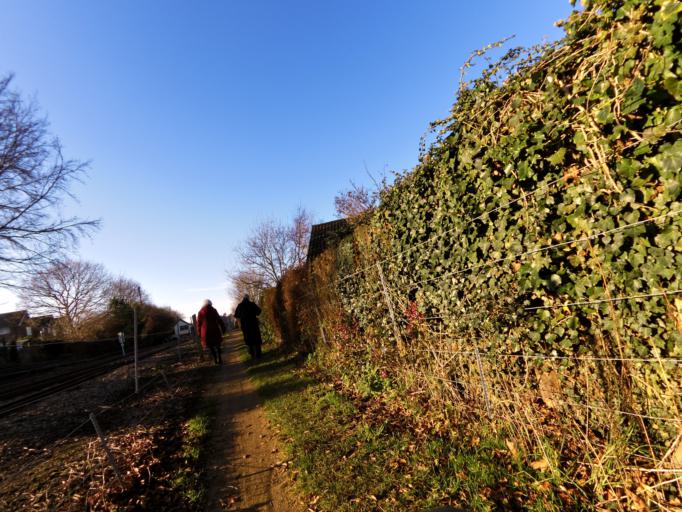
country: GB
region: England
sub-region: Norfolk
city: Aylsham
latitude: 52.7908
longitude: 1.2583
